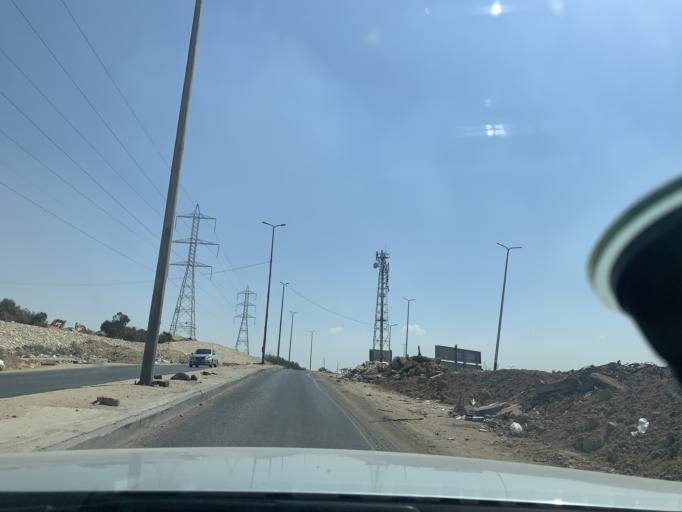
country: EG
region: Muhafazat al Qahirah
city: Cairo
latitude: 30.0251
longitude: 31.3458
